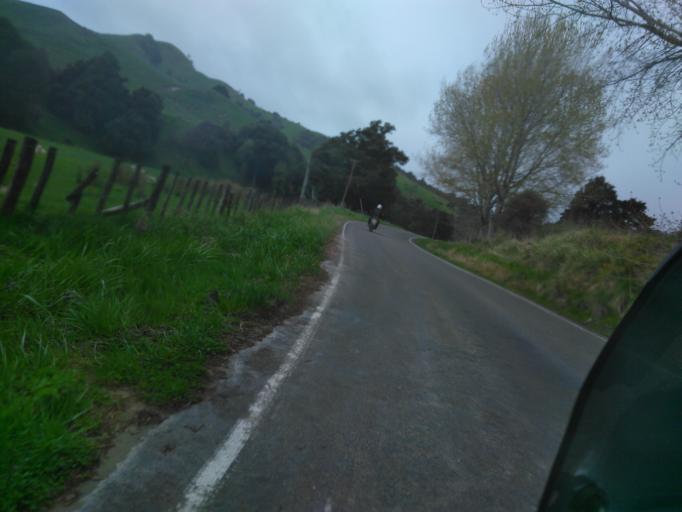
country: NZ
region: Gisborne
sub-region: Gisborne District
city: Gisborne
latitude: -38.6432
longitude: 177.7045
